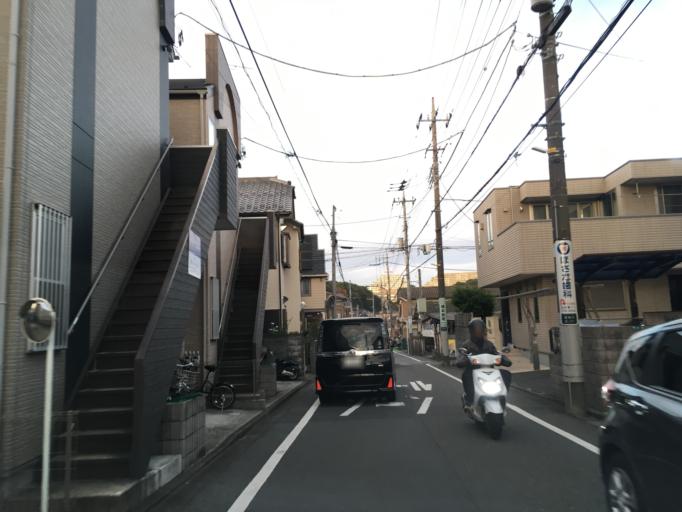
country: JP
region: Tokyo
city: Hachioji
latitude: 35.5984
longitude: 139.3517
